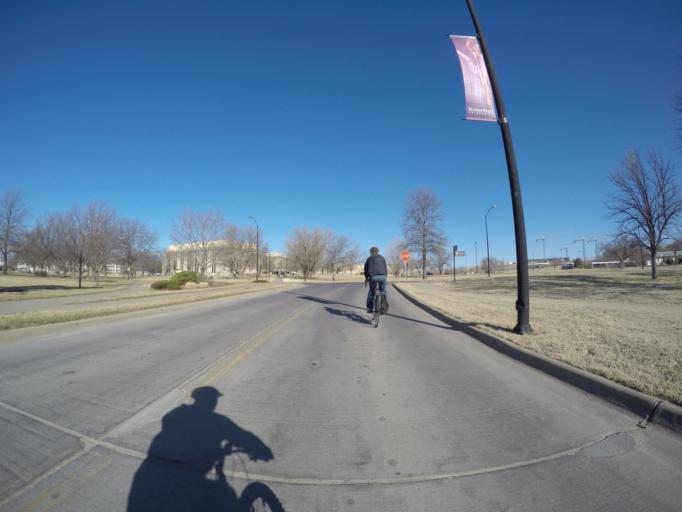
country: US
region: Kansas
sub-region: Riley County
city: Manhattan
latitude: 39.1968
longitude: -96.5824
